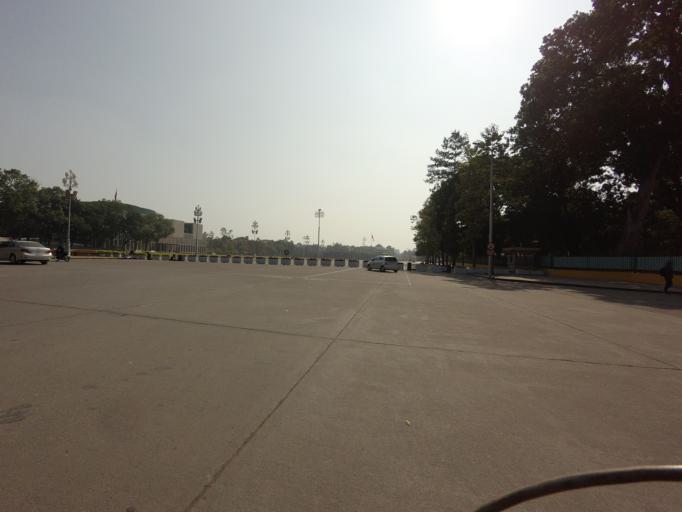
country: VN
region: Ha Noi
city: Hanoi
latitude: 21.0394
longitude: 105.8355
